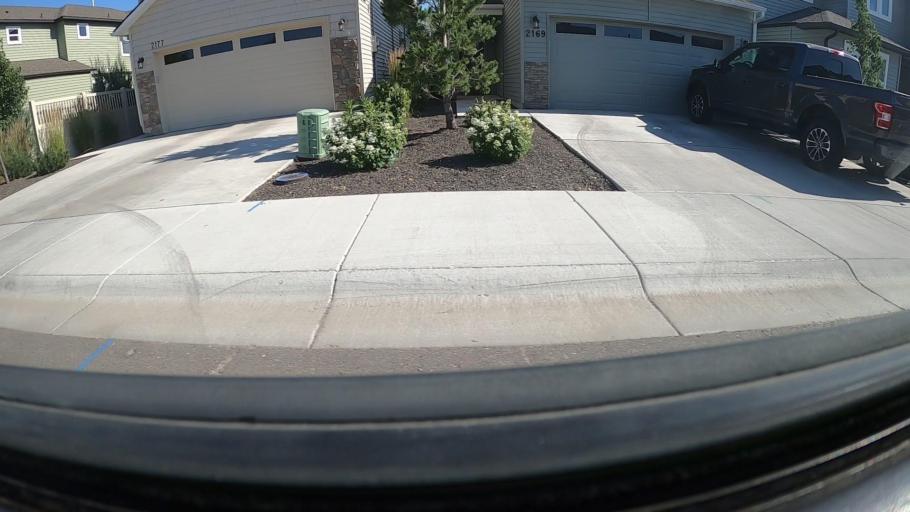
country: US
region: Idaho
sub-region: Ada County
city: Meridian
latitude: 43.6325
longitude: -116.3676
